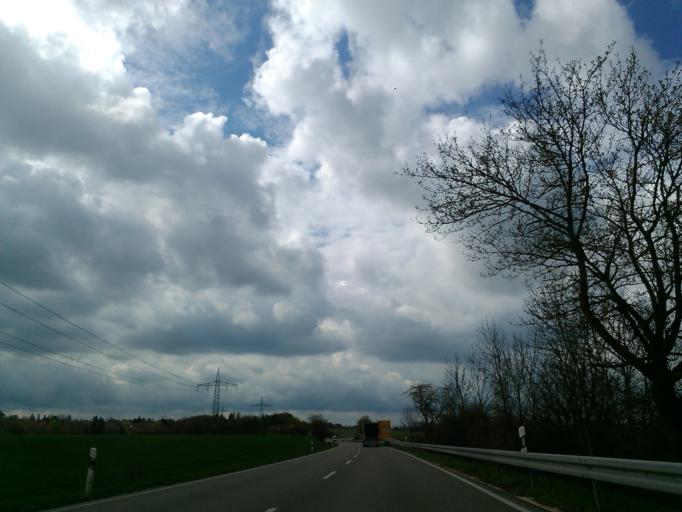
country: DE
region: Baden-Wuerttemberg
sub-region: Tuebingen Region
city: Ulm
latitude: 48.4385
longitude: 10.0133
